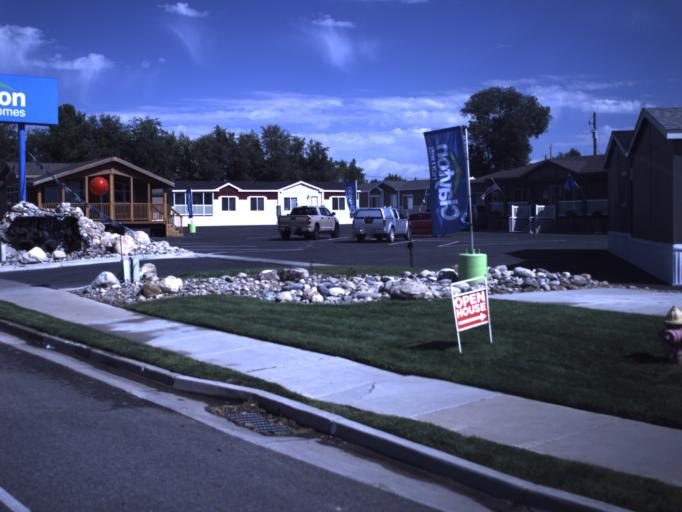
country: US
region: Utah
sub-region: Davis County
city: Hill Air Force Bace
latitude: 41.0841
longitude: -111.9955
